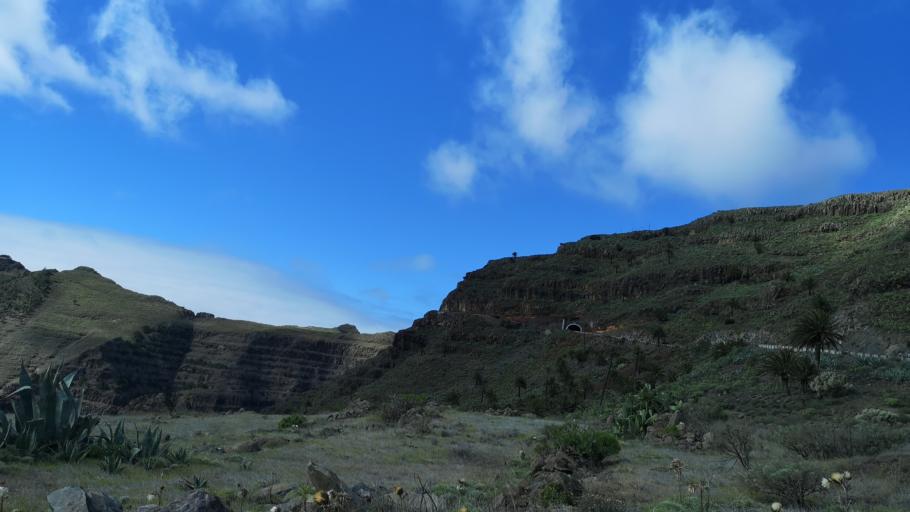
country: ES
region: Canary Islands
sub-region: Provincia de Santa Cruz de Tenerife
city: Vallehermosa
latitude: 28.1199
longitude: -17.3151
